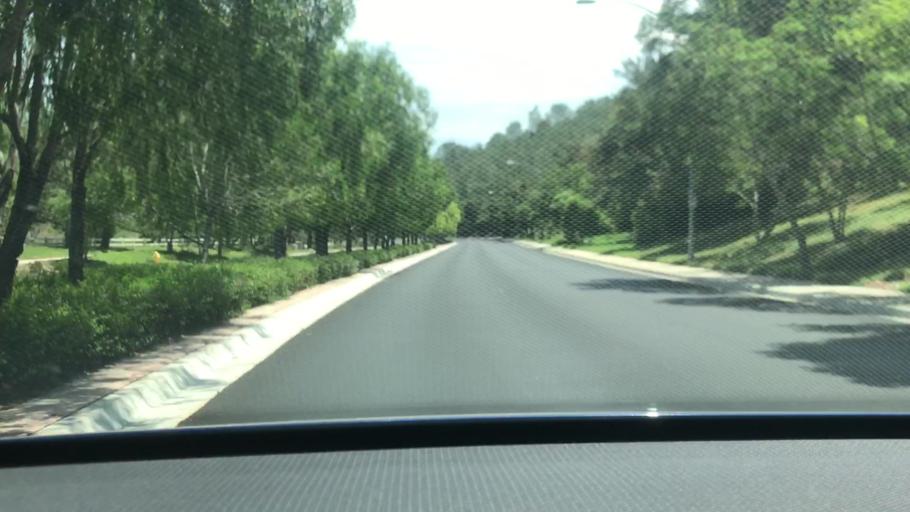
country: US
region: California
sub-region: San Diego County
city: Poway
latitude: 32.9251
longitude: -117.0966
